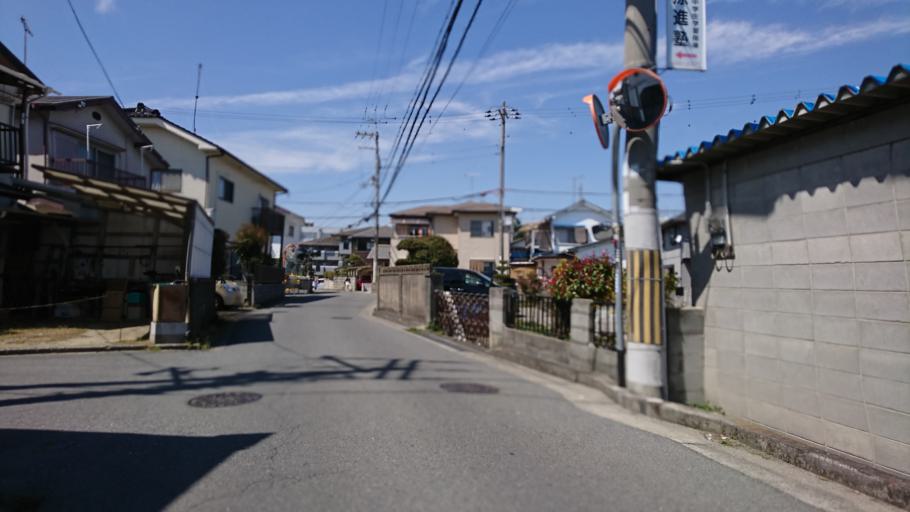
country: JP
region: Hyogo
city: Kakogawacho-honmachi
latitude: 34.7454
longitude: 134.8840
